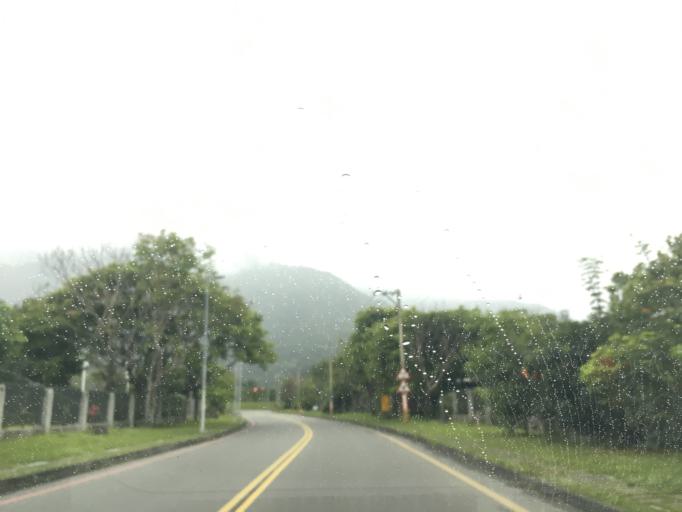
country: TW
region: Taiwan
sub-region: Hualien
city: Hualian
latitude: 24.0002
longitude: 121.5738
